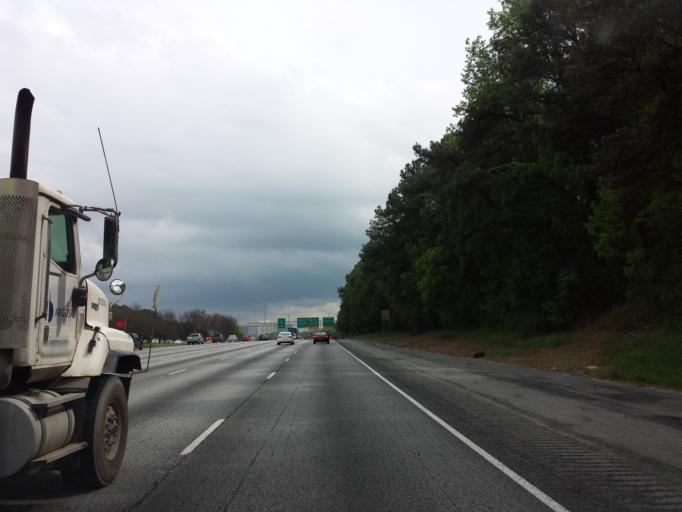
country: US
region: Georgia
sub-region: Cobb County
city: Vinings
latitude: 33.9069
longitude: -84.4768
